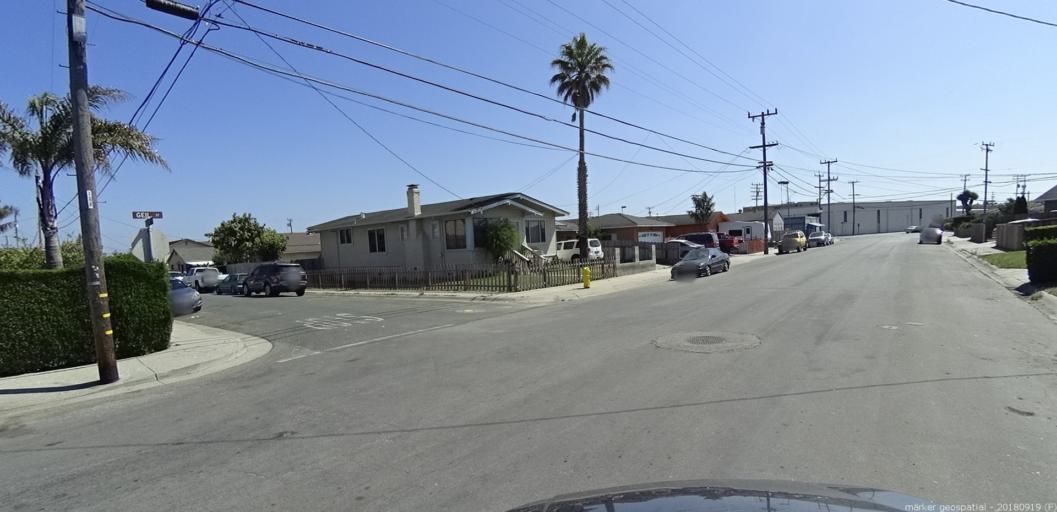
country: US
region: California
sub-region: Monterey County
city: Castroville
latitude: 36.7622
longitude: -121.7479
